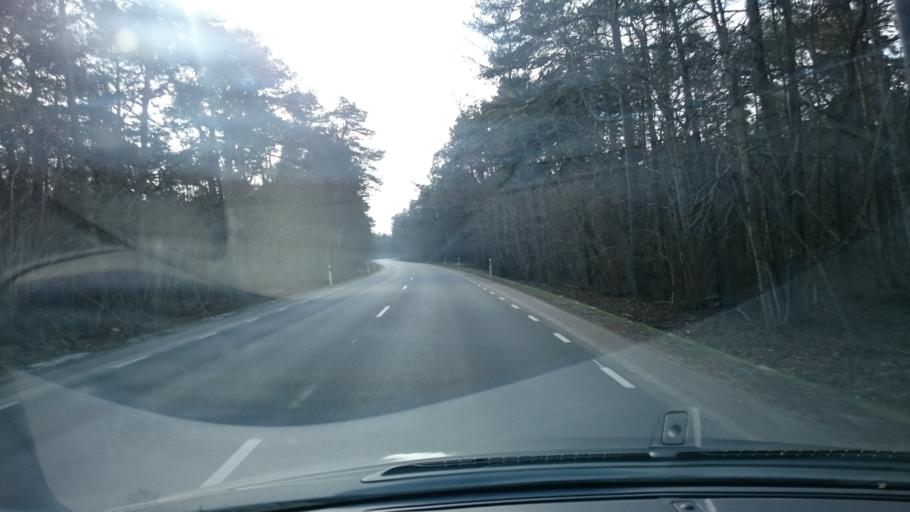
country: EE
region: Harju
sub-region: Paldiski linn
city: Paldiski
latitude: 59.3941
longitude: 24.2422
